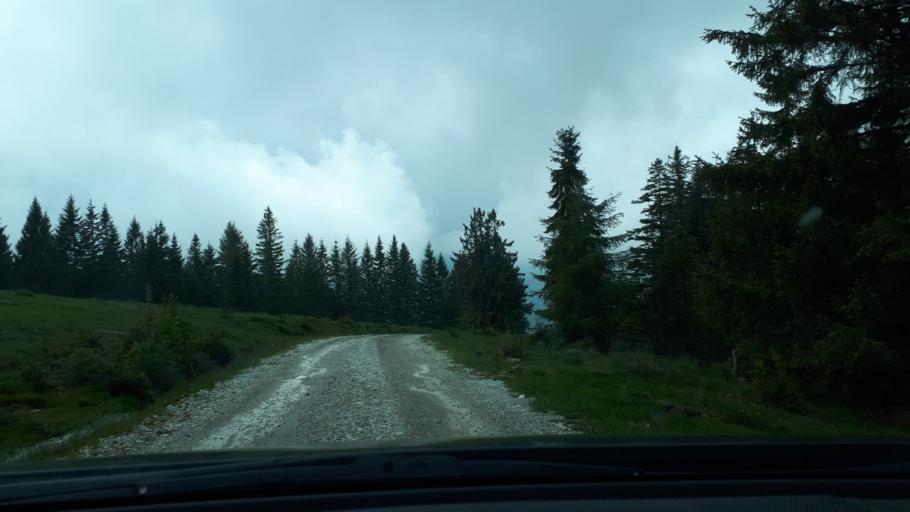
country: AT
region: Styria
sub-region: Politischer Bezirk Deutschlandsberg
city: Kloster
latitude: 46.9093
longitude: 15.0612
